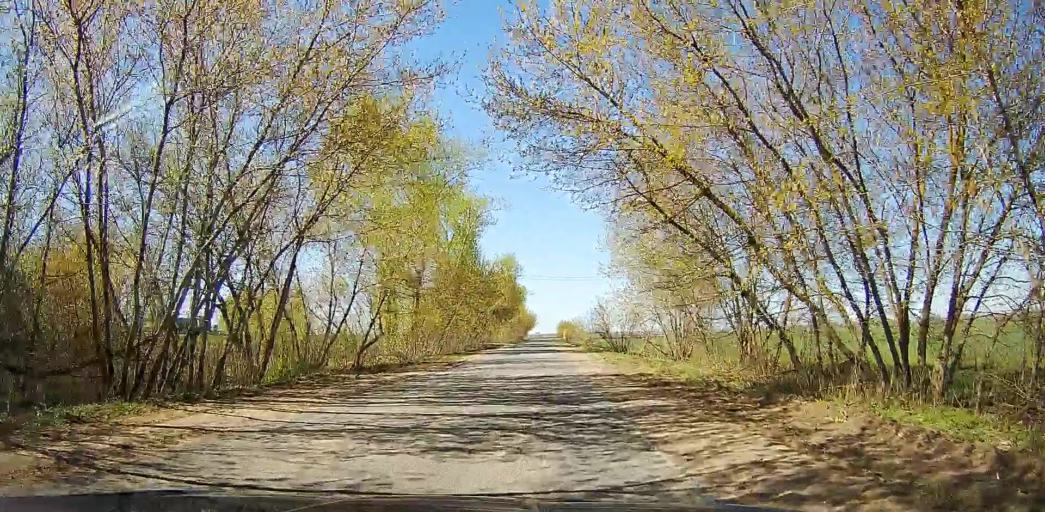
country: RU
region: Moskovskaya
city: Ramenskoye
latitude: 55.4930
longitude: 38.2338
